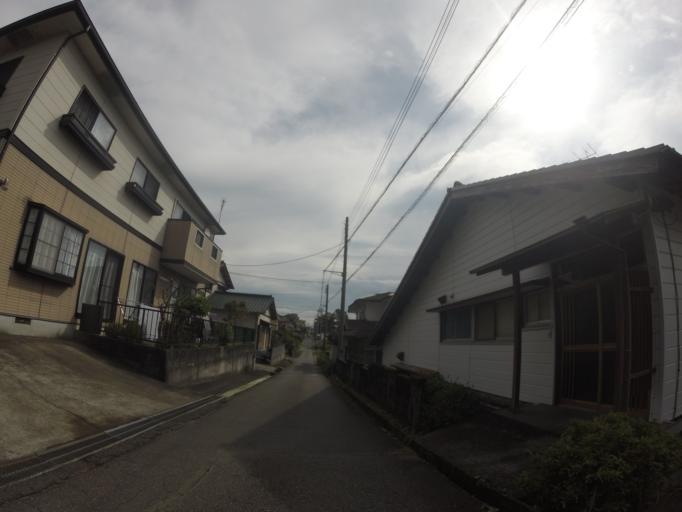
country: JP
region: Shizuoka
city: Fuji
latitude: 35.2210
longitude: 138.6818
